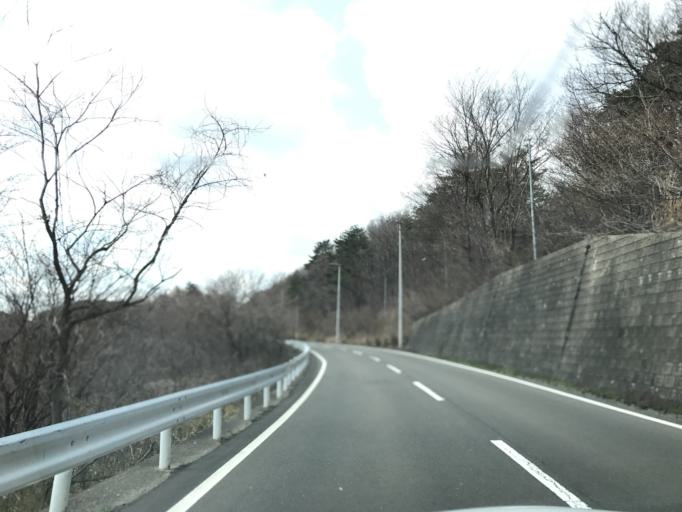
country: JP
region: Miyagi
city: Shiroishi
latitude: 38.0214
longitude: 140.5516
